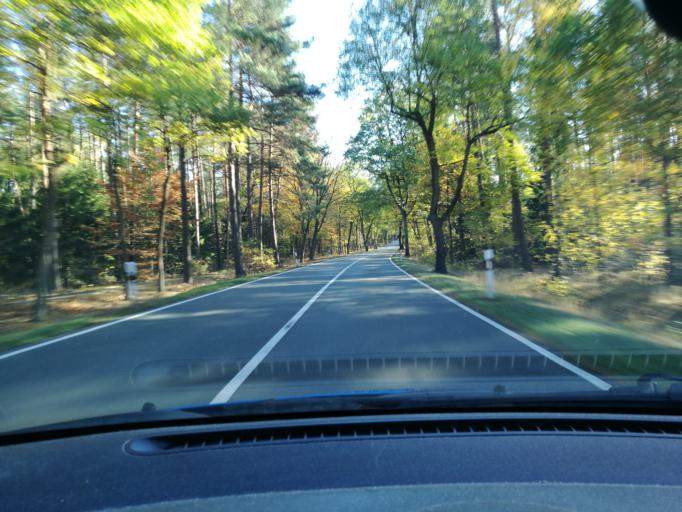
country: DE
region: Lower Saxony
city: Karwitz
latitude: 53.1145
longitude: 11.0074
